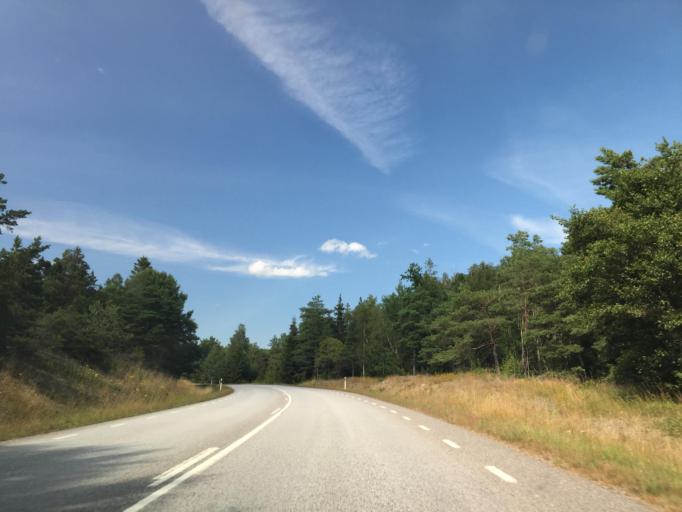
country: SE
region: Vaestra Goetaland
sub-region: Tanums Kommun
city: Tanumshede
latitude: 58.8169
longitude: 11.2630
